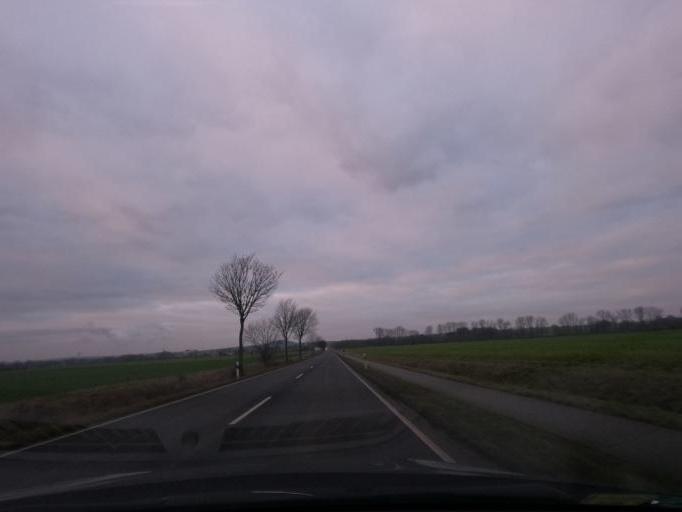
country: DE
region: Lower Saxony
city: Kissenbruck
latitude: 52.1480
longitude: 10.6005
